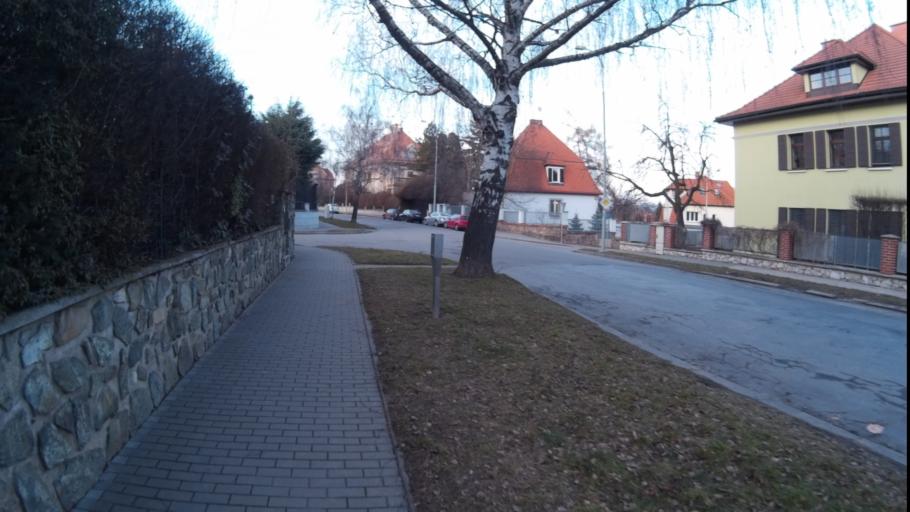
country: CZ
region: South Moravian
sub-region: Mesto Brno
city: Brno
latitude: 49.1960
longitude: 16.5855
